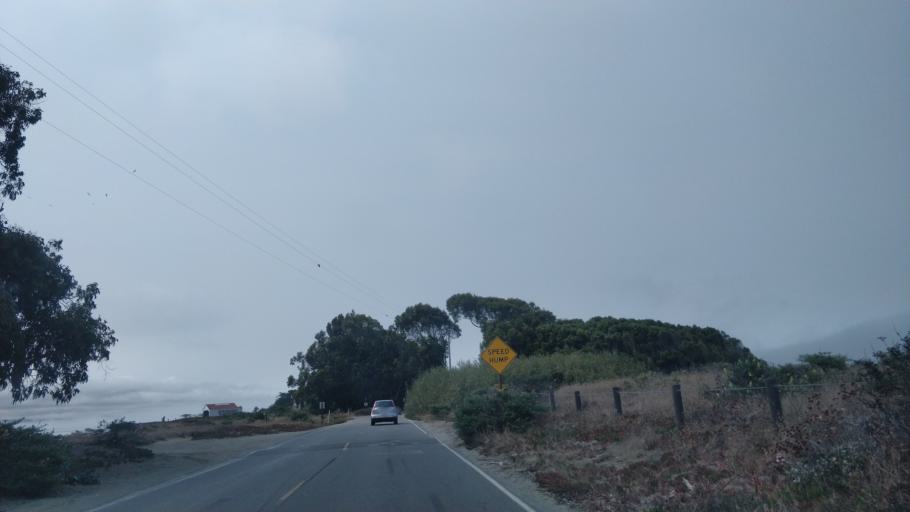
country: US
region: California
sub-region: Humboldt County
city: Bayview
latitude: 40.7713
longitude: -124.2150
